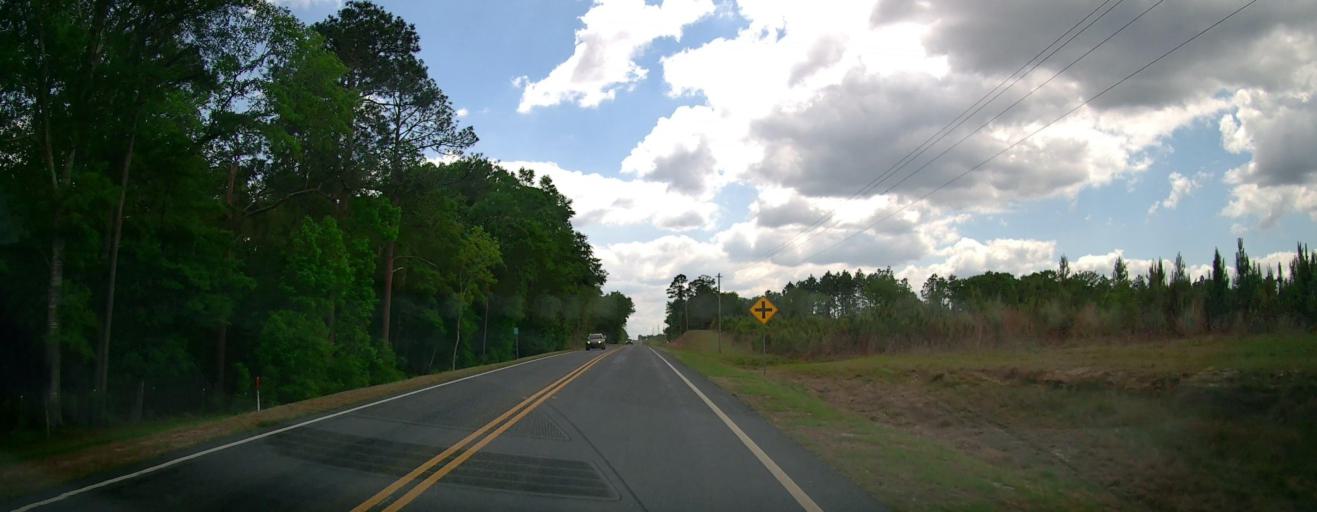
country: US
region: Georgia
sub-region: Treutlen County
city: Soperton
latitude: 32.4469
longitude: -82.6058
